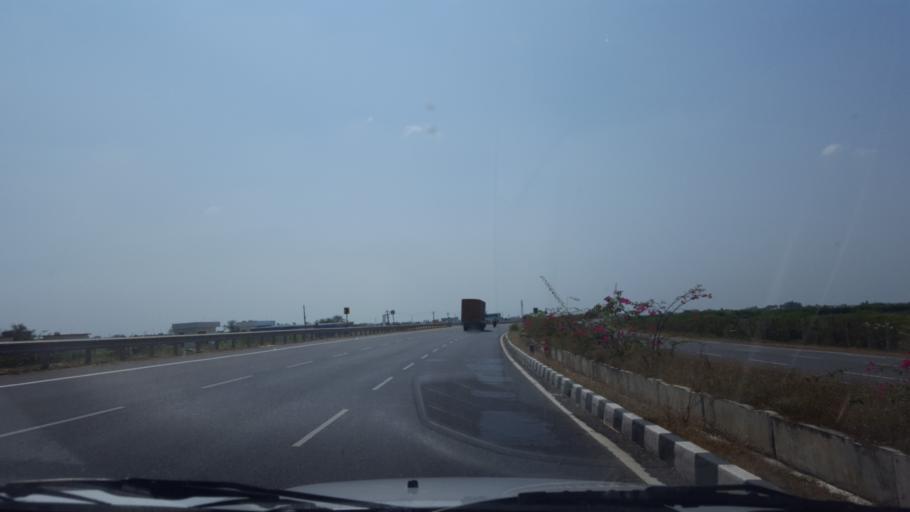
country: IN
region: Andhra Pradesh
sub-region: Prakasam
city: Ongole
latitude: 15.5100
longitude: 80.0734
